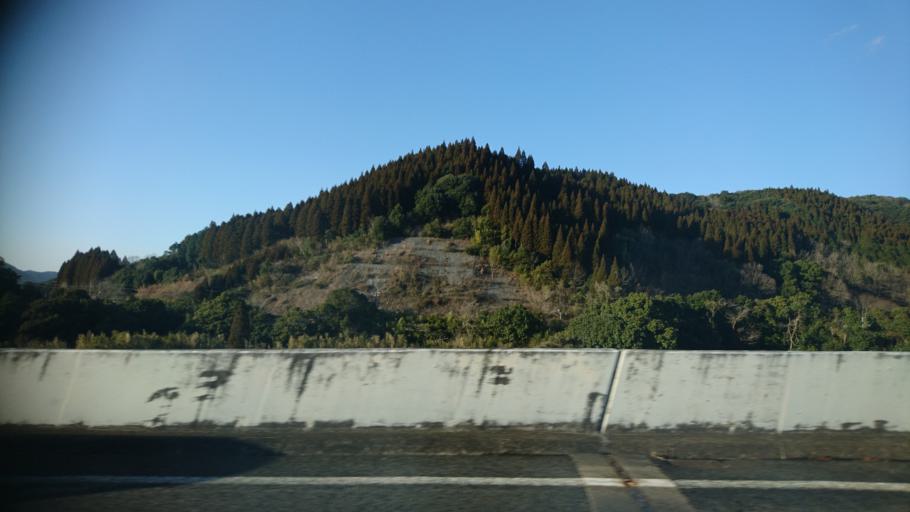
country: JP
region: Miyazaki
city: Miyakonojo
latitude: 31.7917
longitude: 131.1823
